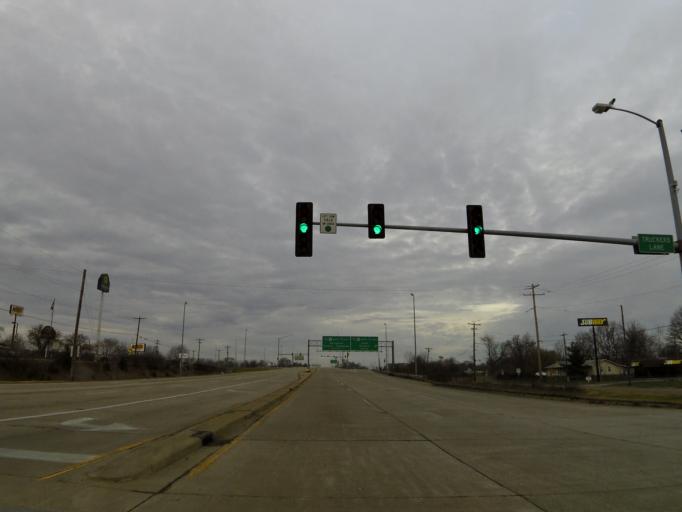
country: US
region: Illinois
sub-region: McLean County
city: Bloomington
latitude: 40.4841
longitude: -89.0231
